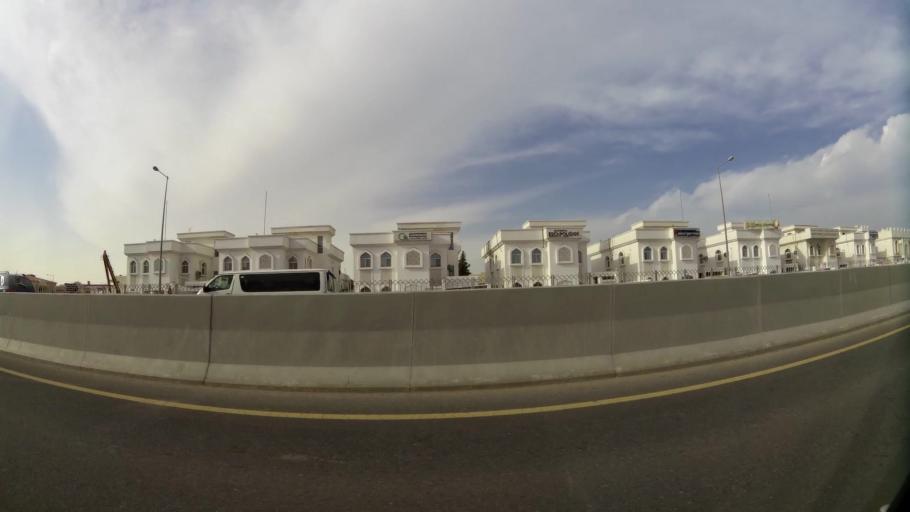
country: QA
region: Baladiyat ad Dawhah
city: Doha
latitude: 25.2544
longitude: 51.5132
